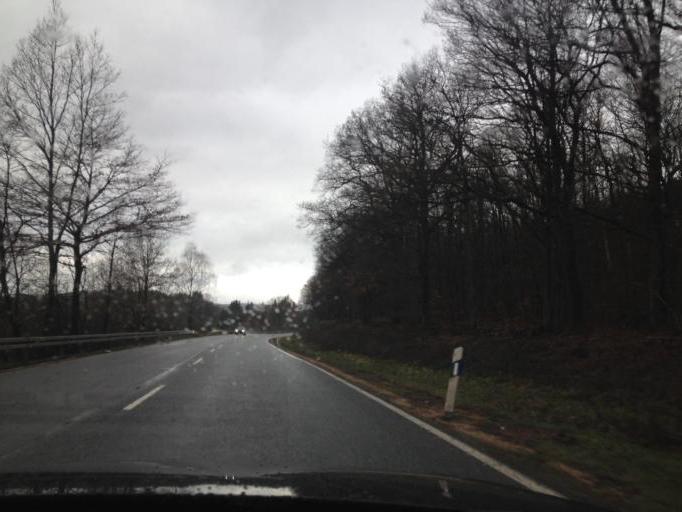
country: DE
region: Saarland
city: Nohfelden
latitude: 49.5800
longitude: 7.1572
